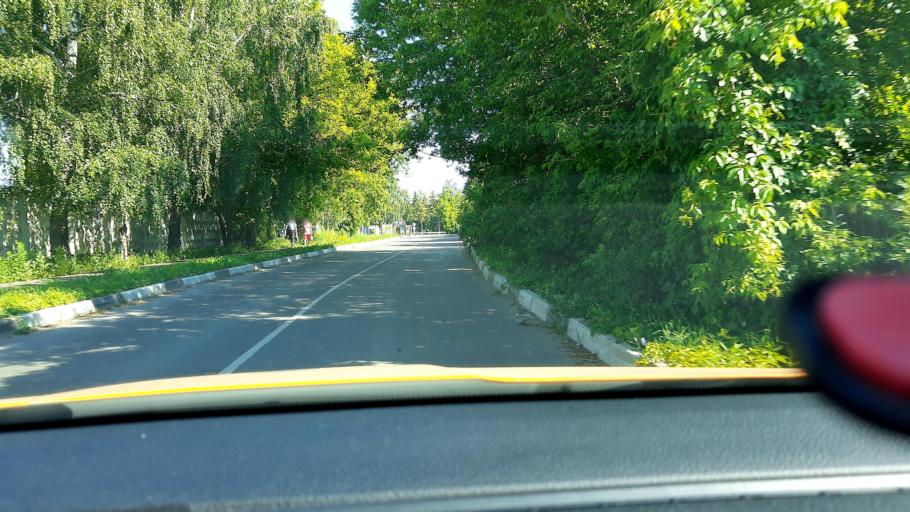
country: RU
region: Moskovskaya
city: Arkhangel'skoye
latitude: 55.7974
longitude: 37.3073
